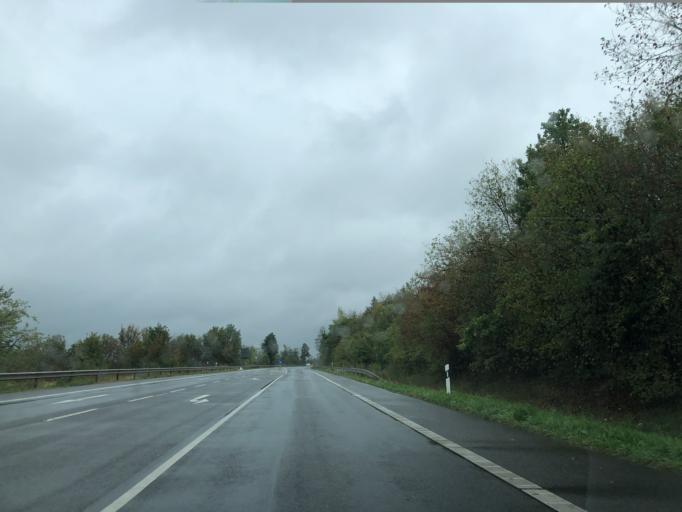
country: DE
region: North Rhine-Westphalia
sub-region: Regierungsbezirk Dusseldorf
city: Grevenbroich
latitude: 51.0803
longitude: 6.5560
